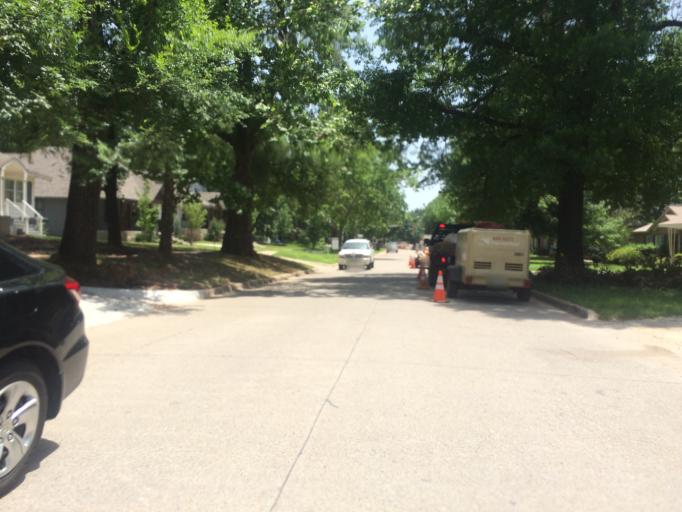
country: US
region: Oklahoma
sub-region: Cleveland County
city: Norman
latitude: 35.2055
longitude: -97.4546
